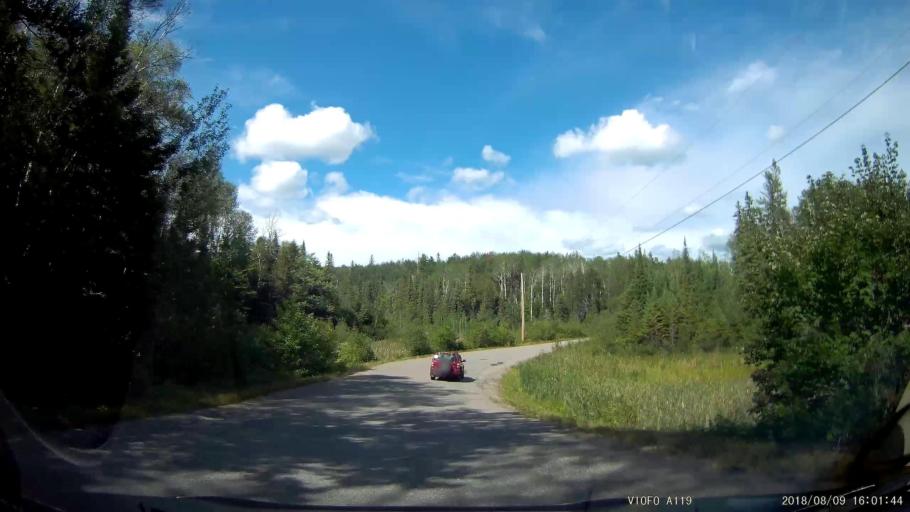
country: CA
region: Ontario
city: Rayside-Balfour
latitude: 46.6154
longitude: -81.4682
